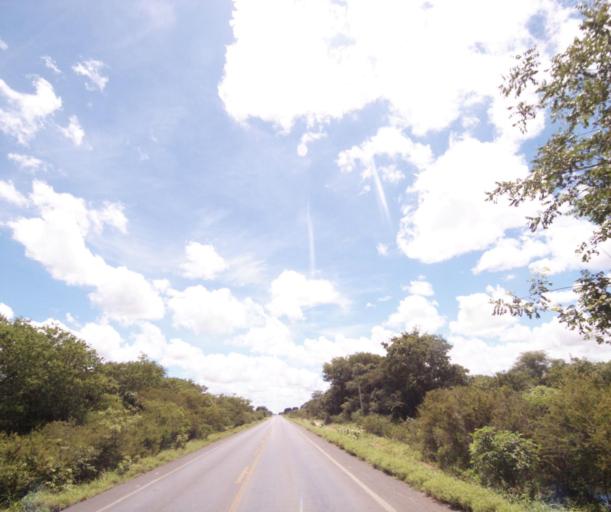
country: BR
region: Bahia
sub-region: Bom Jesus Da Lapa
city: Bom Jesus da Lapa
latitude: -13.2616
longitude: -43.5243
